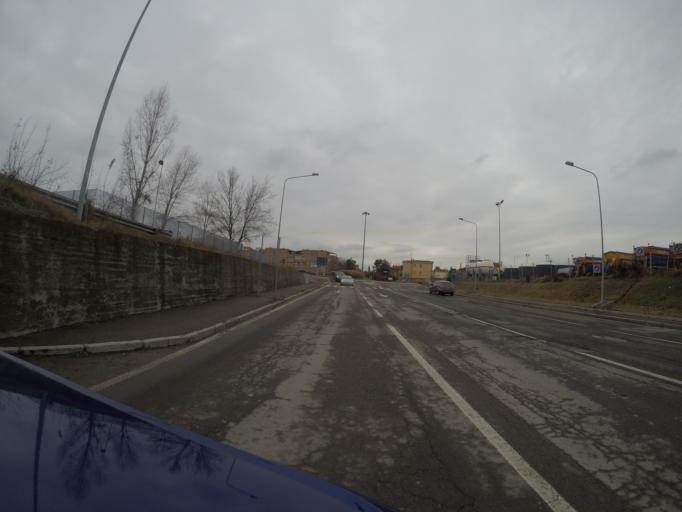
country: IT
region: Emilia-Romagna
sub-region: Provincia di Bologna
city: Trebbo
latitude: 44.5237
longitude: 11.2965
